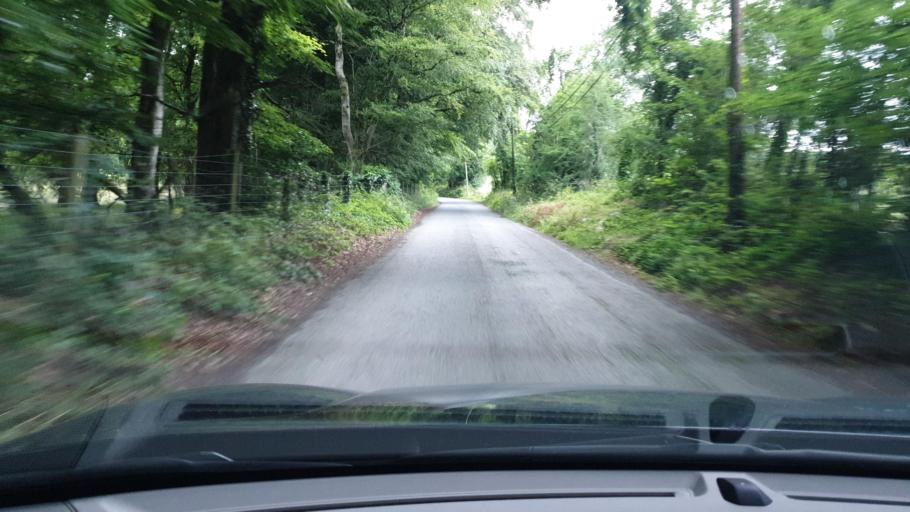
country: IE
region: Leinster
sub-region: South Dublin
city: Rathcoole
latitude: 53.2157
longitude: -6.4790
